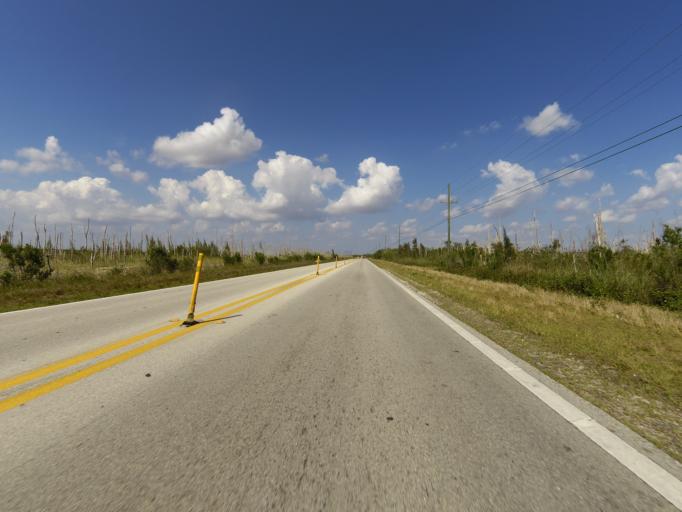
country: US
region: Florida
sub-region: Miami-Dade County
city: Palm Springs North
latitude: 25.9304
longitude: -80.4494
